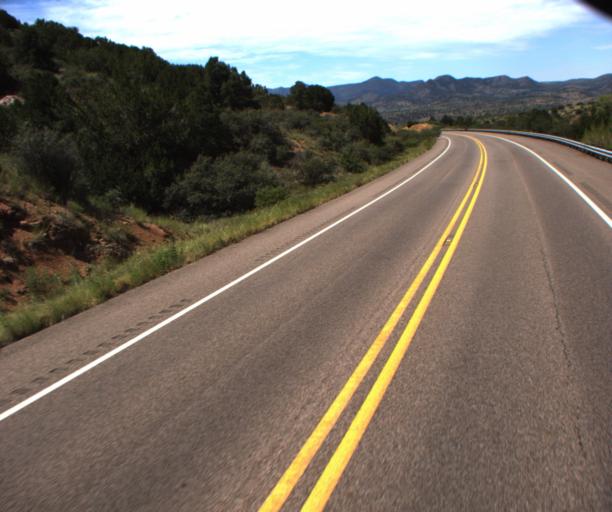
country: US
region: Arizona
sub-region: Gila County
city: Globe
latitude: 33.6111
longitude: -110.6231
